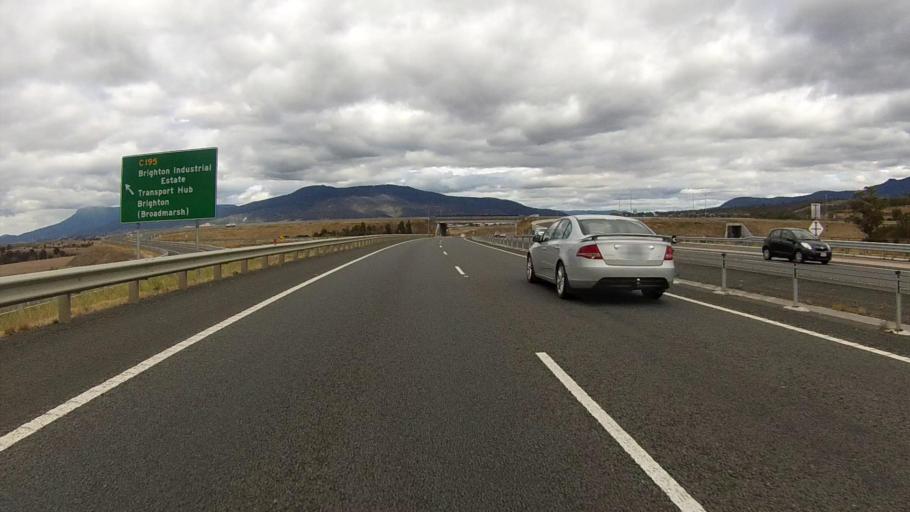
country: AU
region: Tasmania
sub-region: Brighton
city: Bridgewater
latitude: -42.7122
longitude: 147.2470
